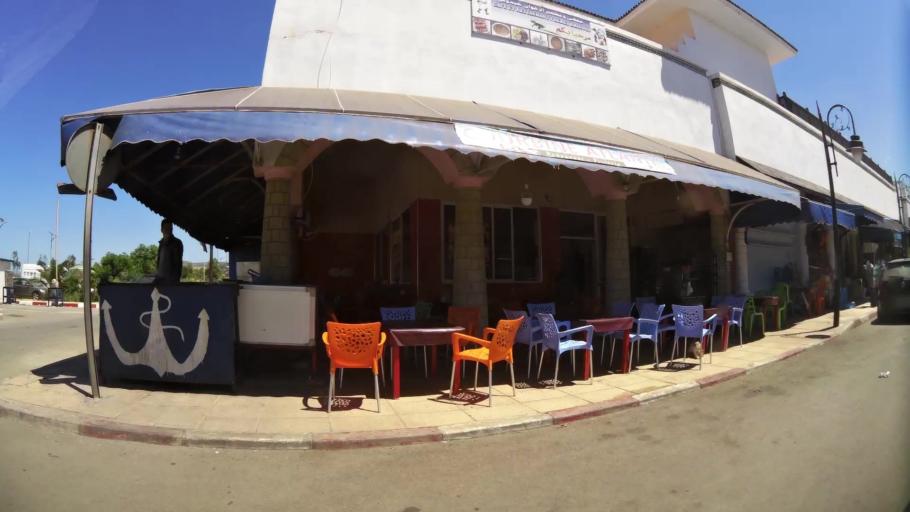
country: MA
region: Oriental
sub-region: Berkane-Taourirt
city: Madagh
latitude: 35.0815
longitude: -2.2147
